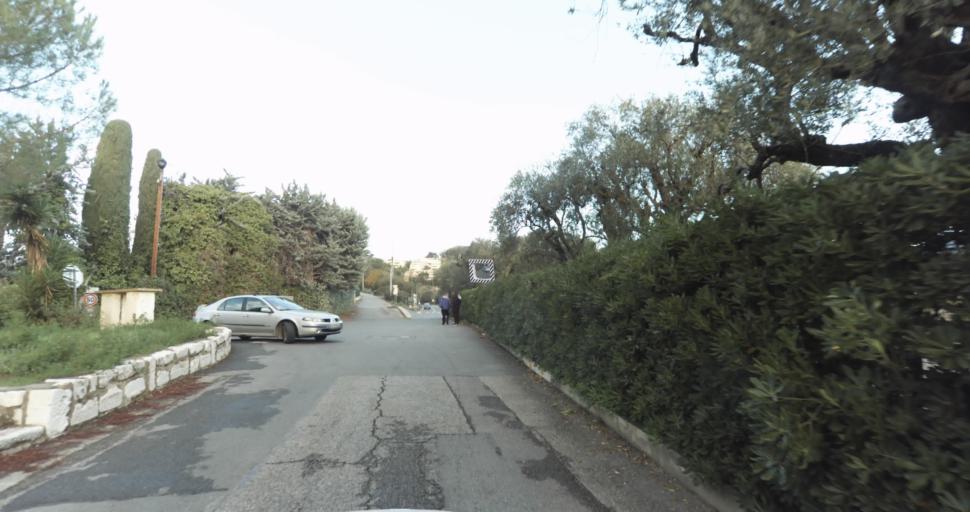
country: FR
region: Provence-Alpes-Cote d'Azur
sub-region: Departement des Alpes-Maritimes
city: Vence
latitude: 43.7135
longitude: 7.1268
